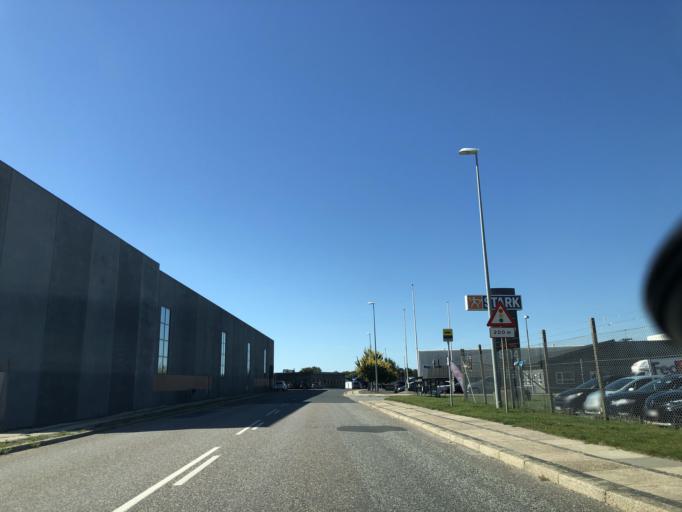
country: DK
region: North Denmark
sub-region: Mariagerfjord Kommune
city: Hobro
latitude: 56.6494
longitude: 9.7985
